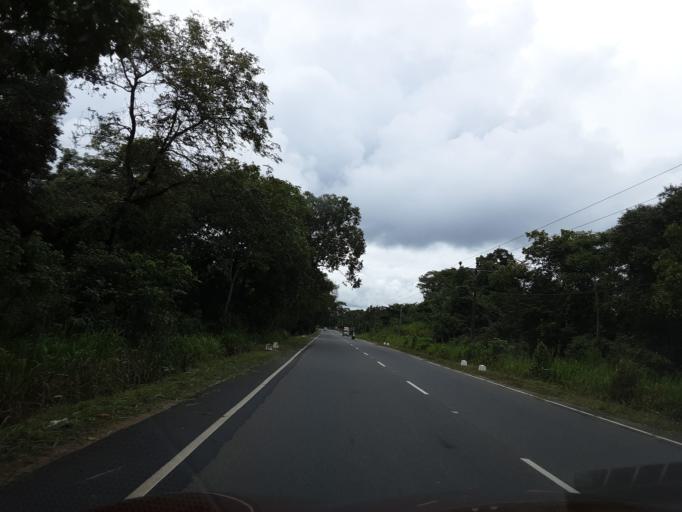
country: LK
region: Uva
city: Badulla
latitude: 7.3989
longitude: 81.1056
